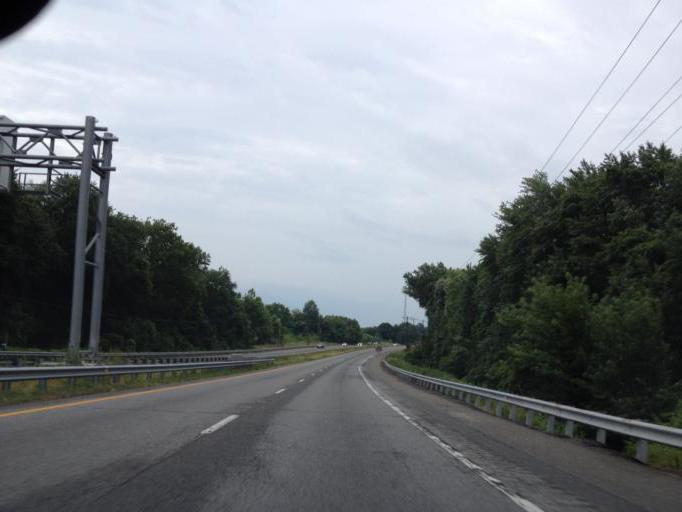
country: US
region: Maryland
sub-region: Queen Anne's County
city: Centreville
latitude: 38.9510
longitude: -76.0687
